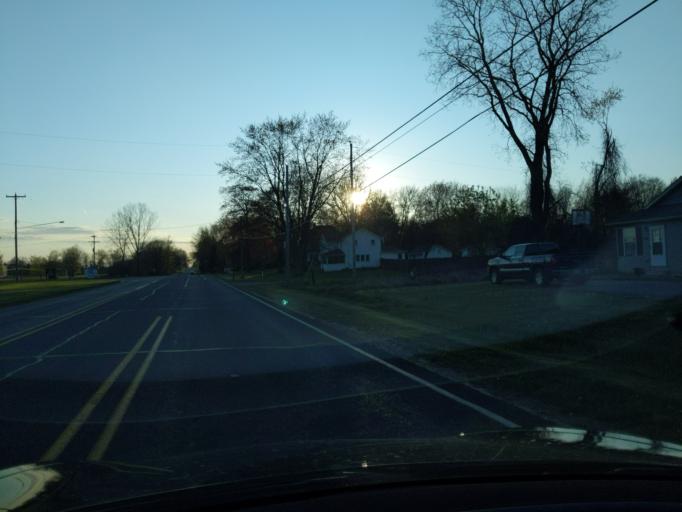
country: US
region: Michigan
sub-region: Jackson County
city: Jackson
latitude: 42.2766
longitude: -84.4760
